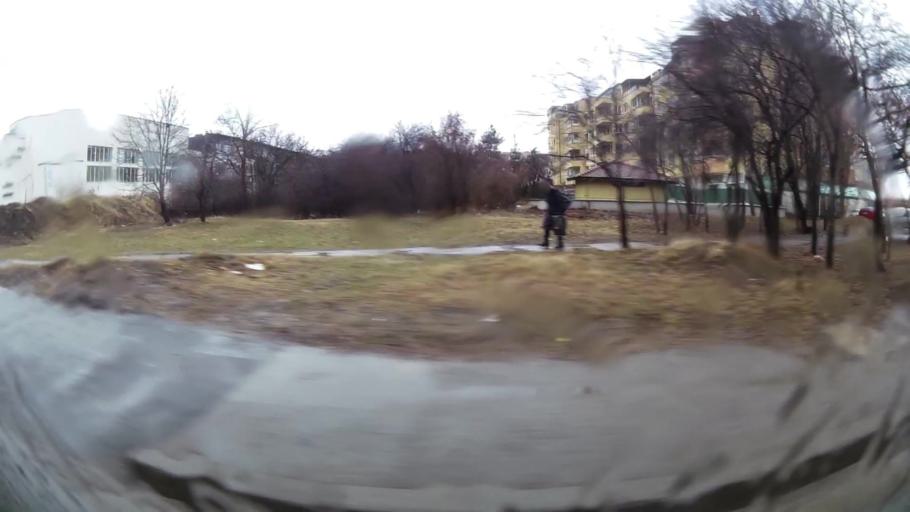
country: BG
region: Sofia-Capital
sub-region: Stolichna Obshtina
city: Sofia
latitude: 42.6646
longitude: 23.3644
